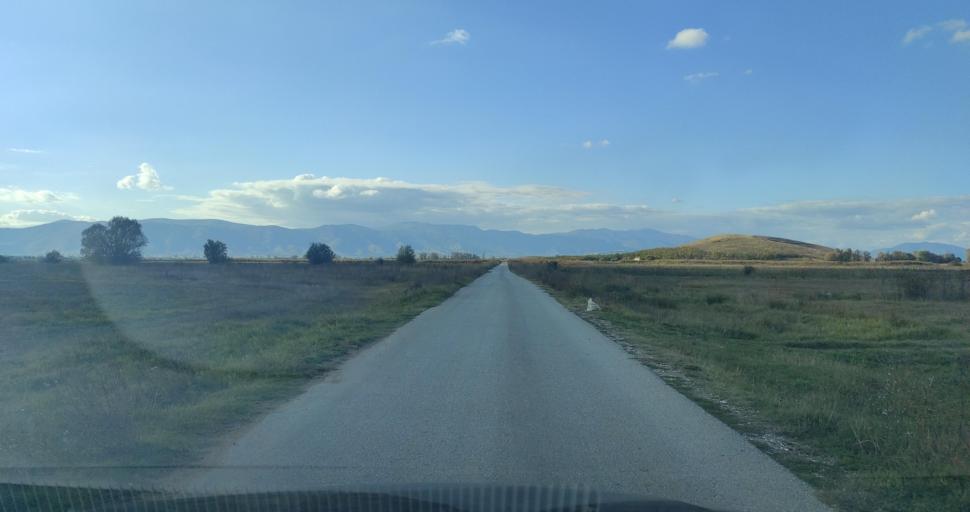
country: MK
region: Prilep
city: Topolcani
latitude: 41.2789
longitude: 21.4282
